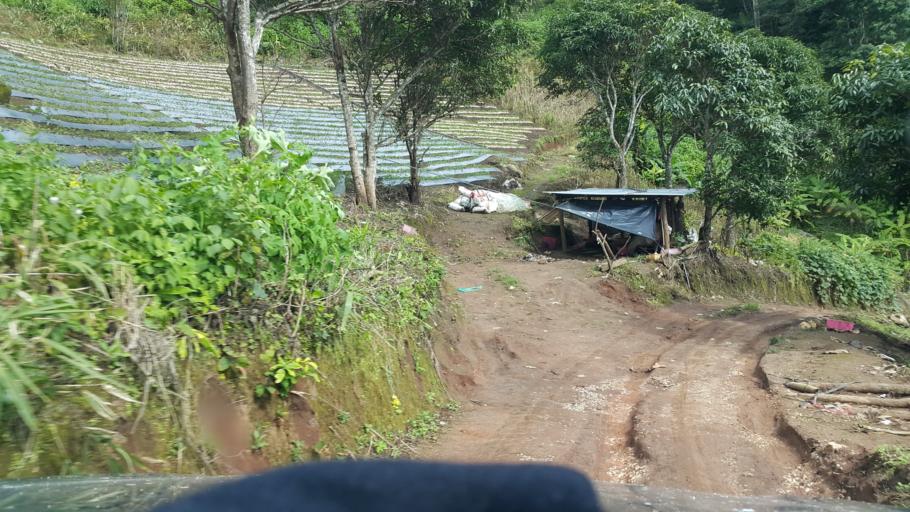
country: TH
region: Chiang Mai
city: Samoeng
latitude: 18.8682
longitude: 98.4952
